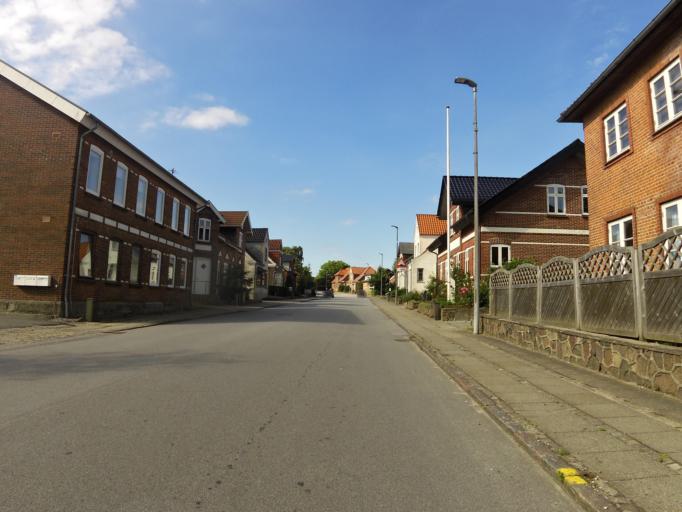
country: DK
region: South Denmark
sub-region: Vejen Kommune
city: Rodding
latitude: 55.3692
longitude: 9.0594
